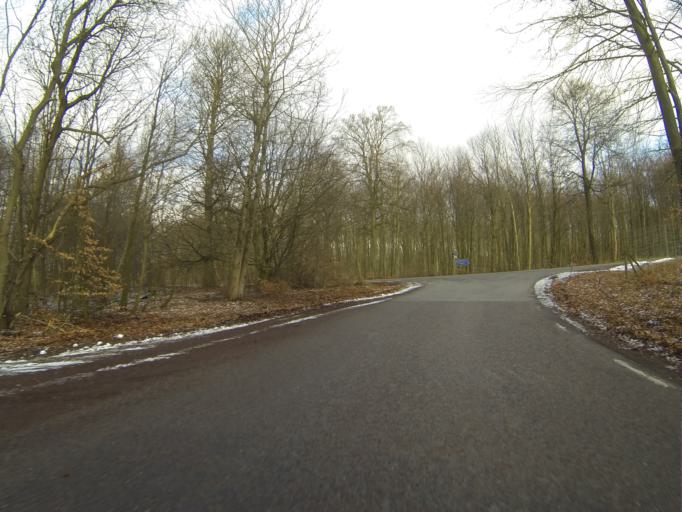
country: SE
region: Skane
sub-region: Svedala Kommun
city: Svedala
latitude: 55.5367
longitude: 13.2766
